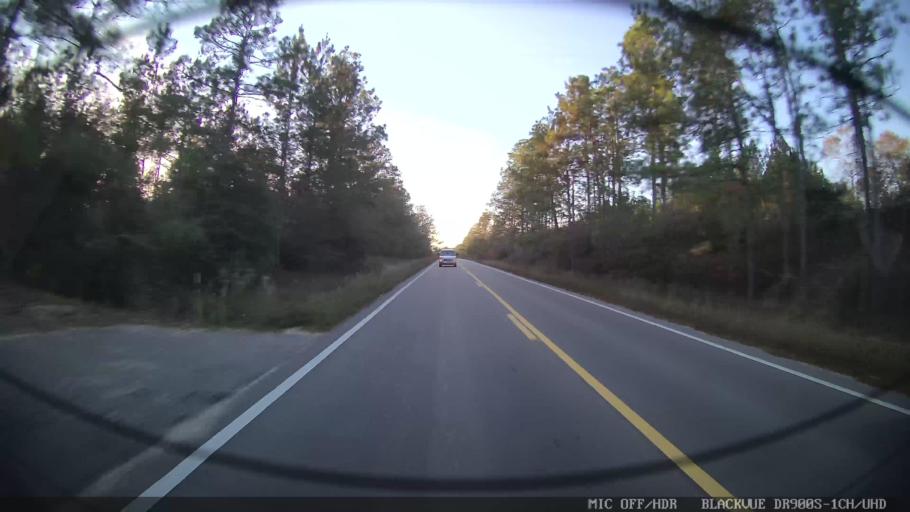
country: US
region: Mississippi
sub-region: Lamar County
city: Lumberton
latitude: 30.9992
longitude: -89.3028
